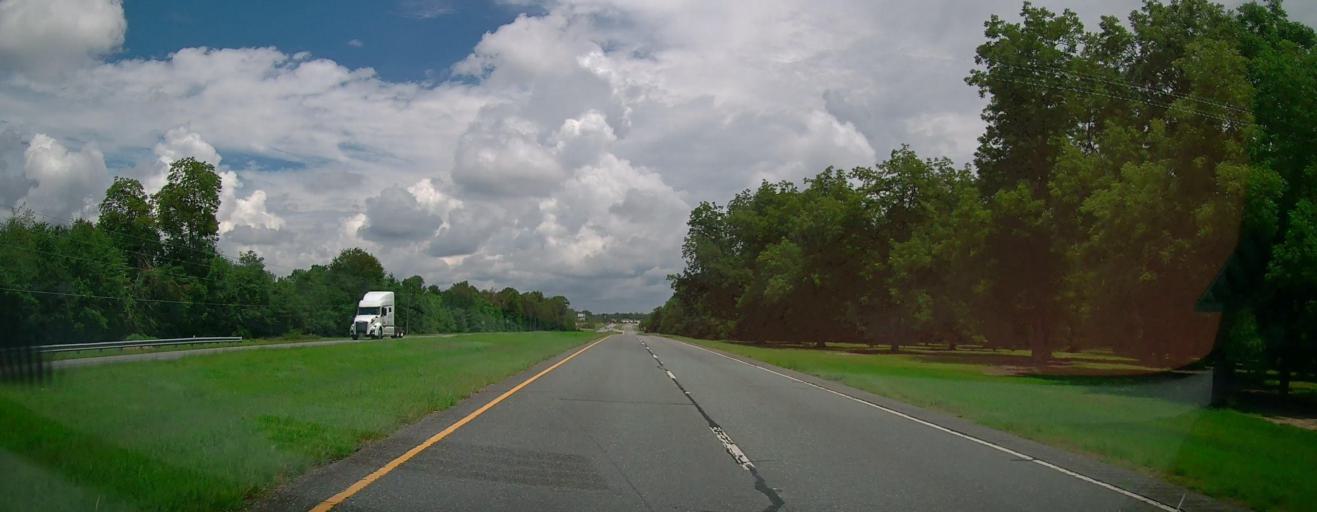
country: US
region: Georgia
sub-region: Dodge County
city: Eastman
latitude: 32.1768
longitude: -83.1754
